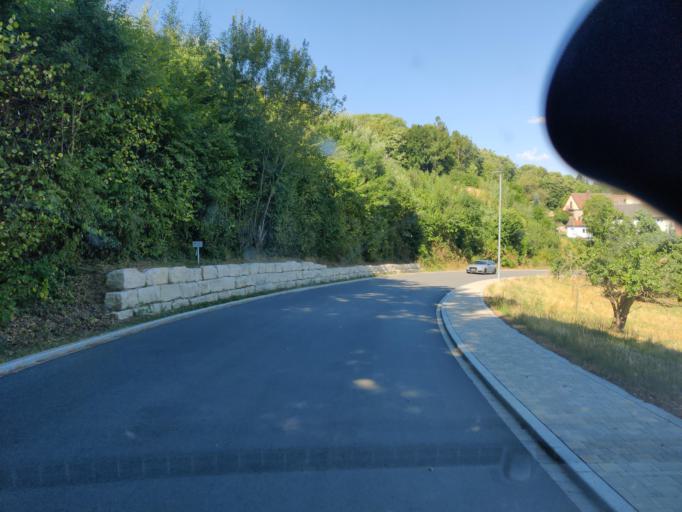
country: DE
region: Bavaria
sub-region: Regierungsbezirk Mittelfranken
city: Bergen
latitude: 49.0706
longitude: 11.0860
